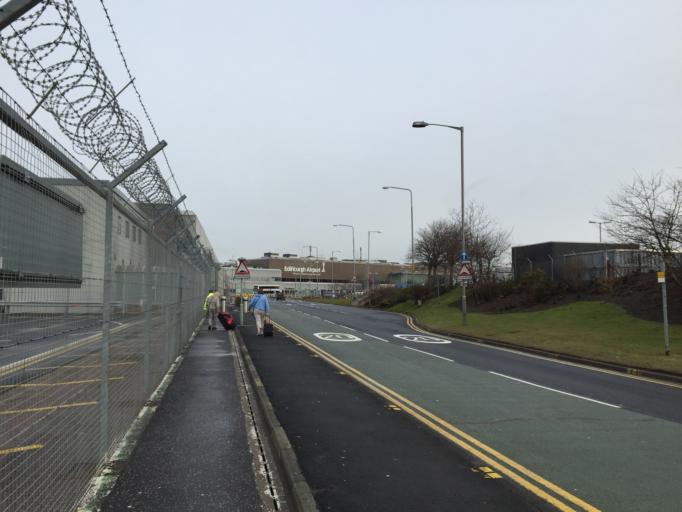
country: GB
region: Scotland
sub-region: Edinburgh
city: Ratho
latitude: 55.9459
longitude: -3.3650
